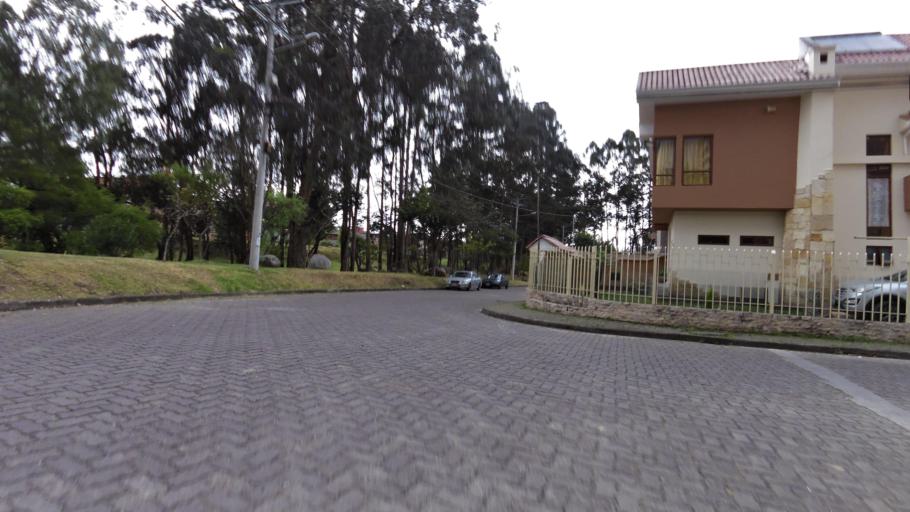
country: EC
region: Azuay
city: Cuenca
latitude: -2.9187
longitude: -79.0224
